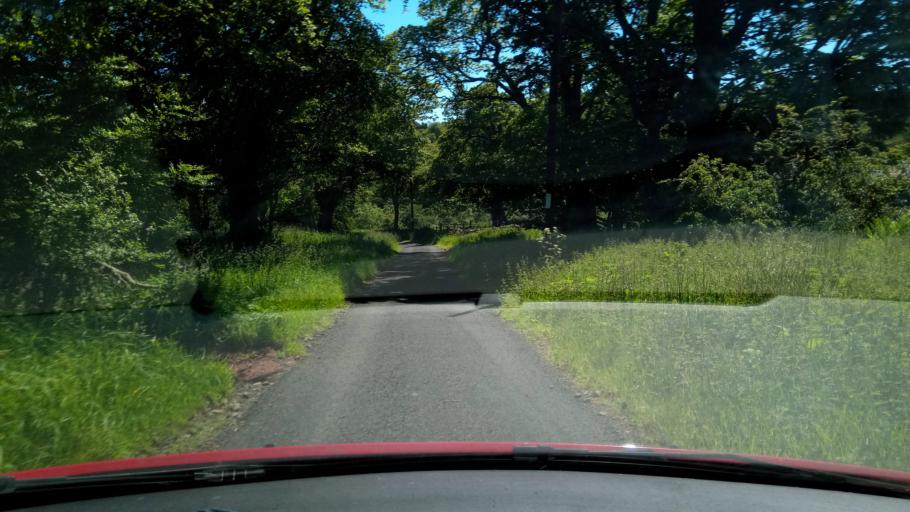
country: GB
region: Scotland
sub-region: The Scottish Borders
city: Duns
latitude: 55.8085
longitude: -2.4978
